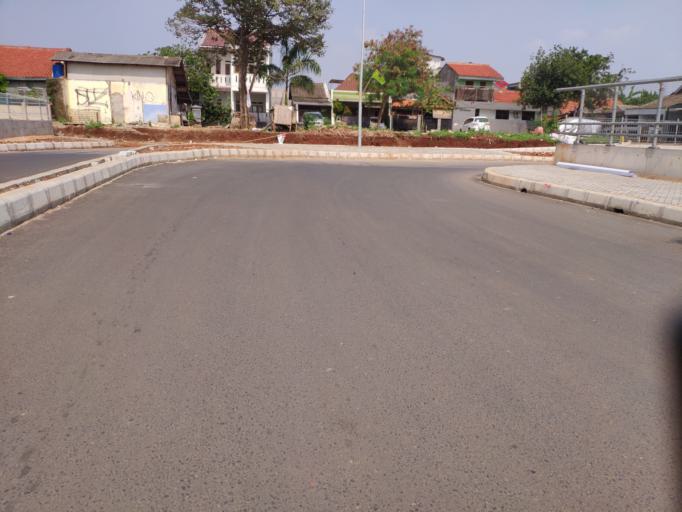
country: ID
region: West Java
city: Pamulang
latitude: -6.3317
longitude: 106.8000
